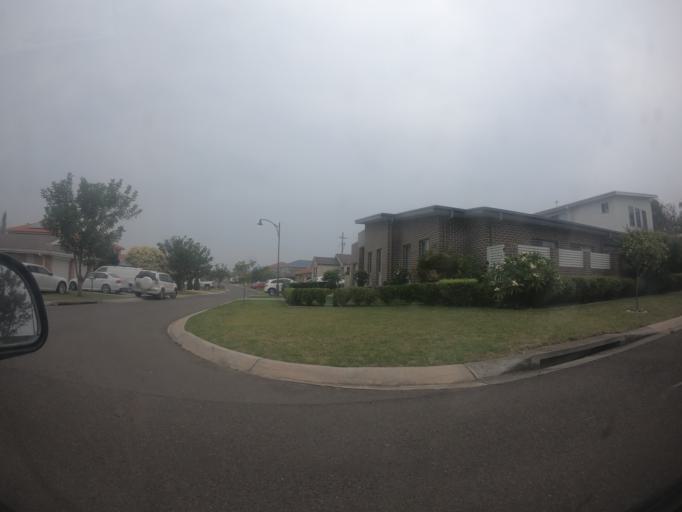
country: AU
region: New South Wales
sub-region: Shellharbour
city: Croom
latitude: -34.5916
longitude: 150.8498
